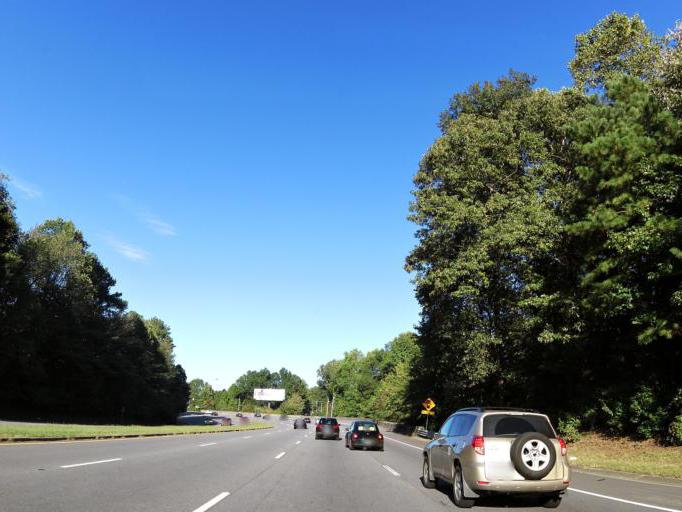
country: US
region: Georgia
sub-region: Cobb County
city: Marietta
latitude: 33.9428
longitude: -84.5007
